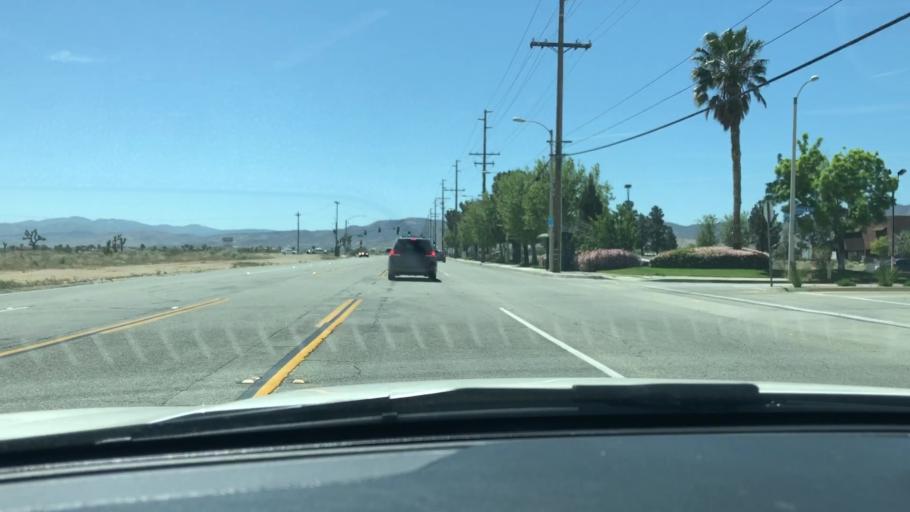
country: US
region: California
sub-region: Los Angeles County
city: Desert View Highlands
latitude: 34.6333
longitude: -118.1478
